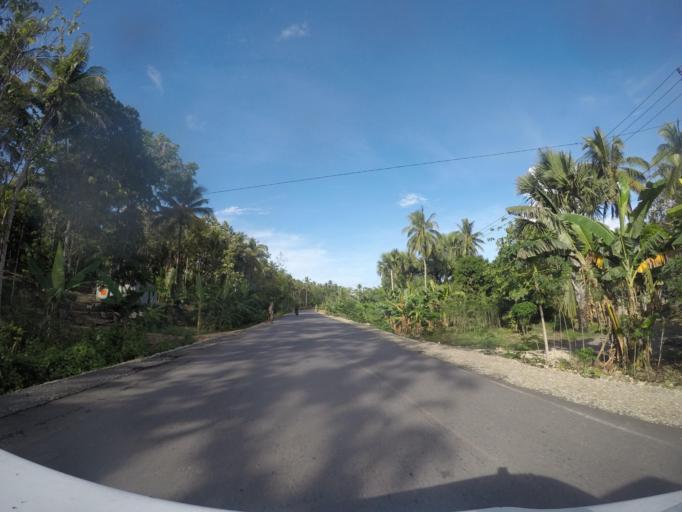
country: TL
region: Baucau
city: Baucau
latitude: -8.4978
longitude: 126.4524
